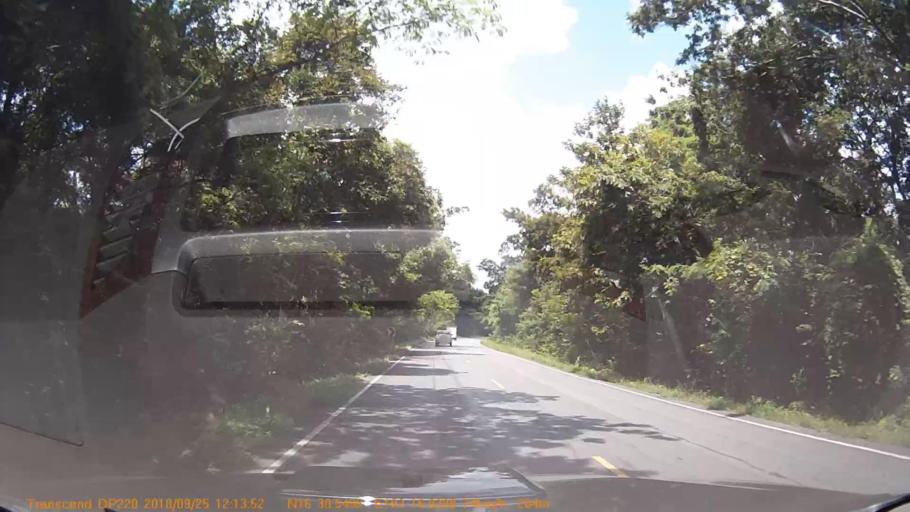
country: TH
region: Kalasin
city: Huai Mek
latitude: 16.5092
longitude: 103.2673
